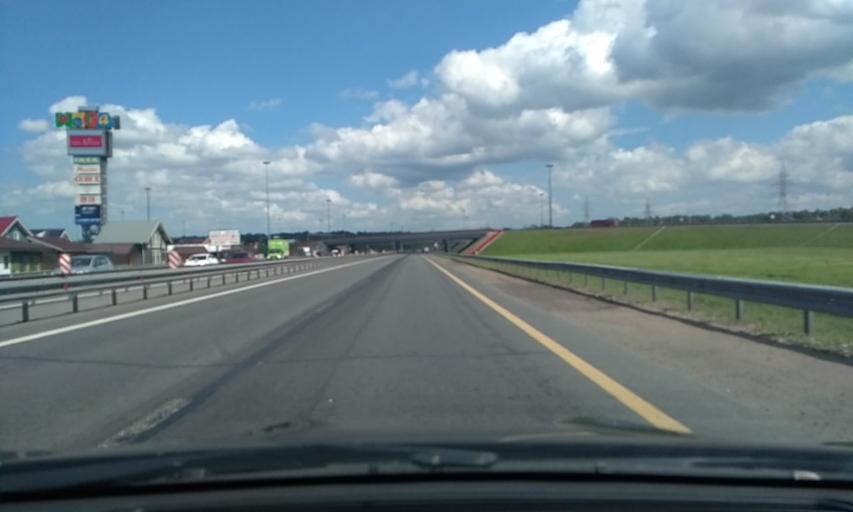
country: RU
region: Leningrad
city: Rybatskoye
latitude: 59.8899
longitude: 30.5156
